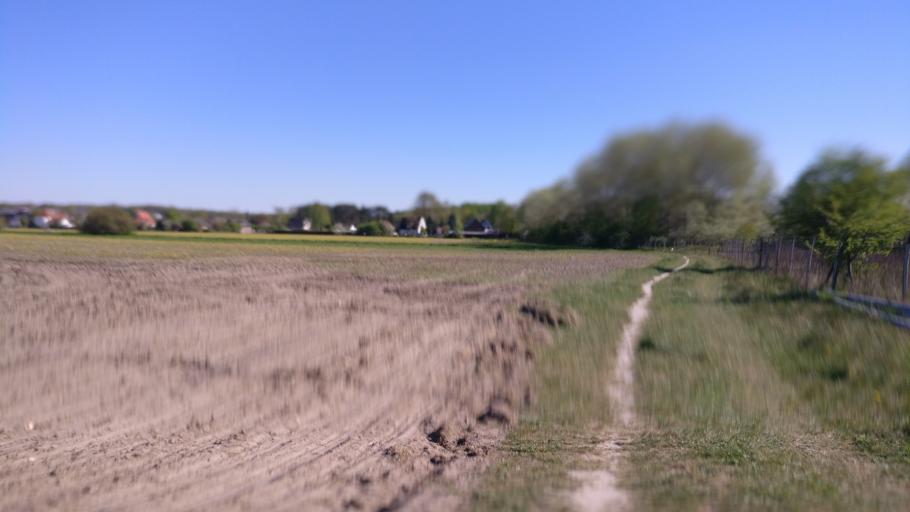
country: DE
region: North Rhine-Westphalia
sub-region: Regierungsbezirk Detmold
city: Lage
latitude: 52.0188
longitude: 8.7592
